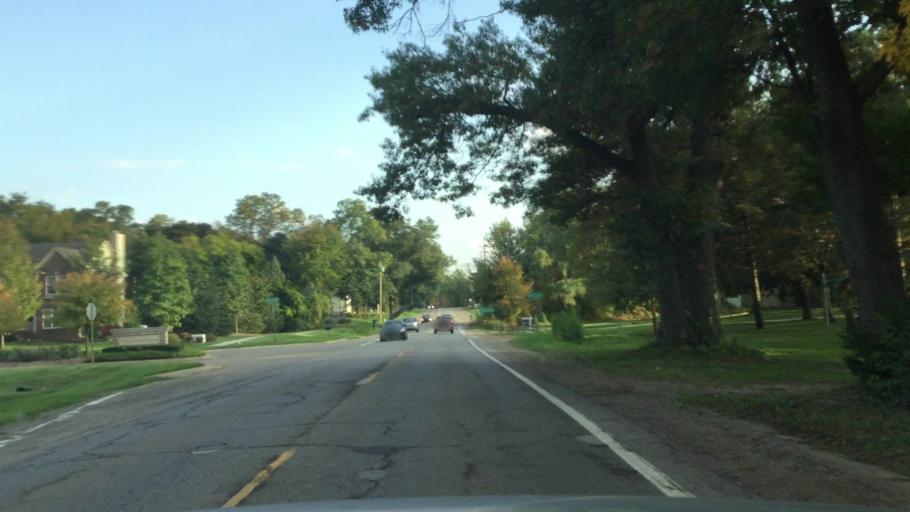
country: US
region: Michigan
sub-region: Oakland County
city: Wolverine Lake
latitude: 42.6315
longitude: -83.4631
